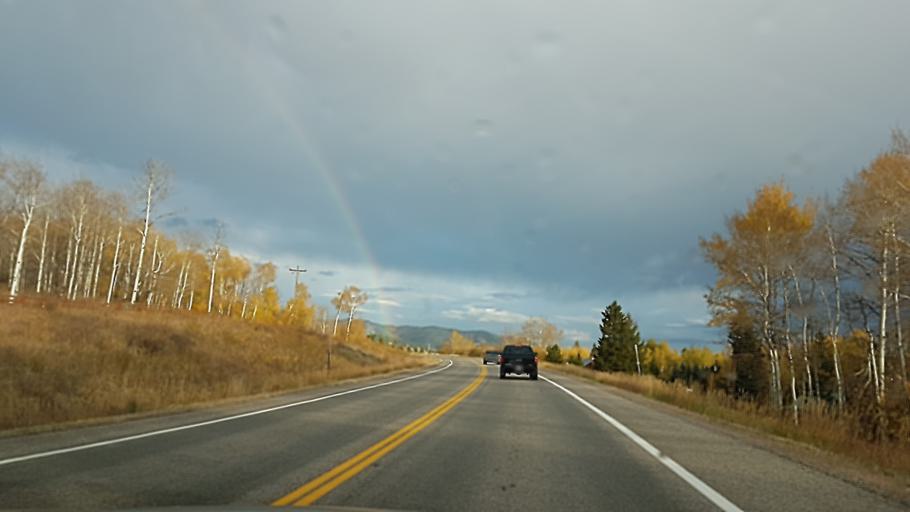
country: US
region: Montana
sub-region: Gallatin County
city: West Yellowstone
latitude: 44.6686
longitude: -111.3987
